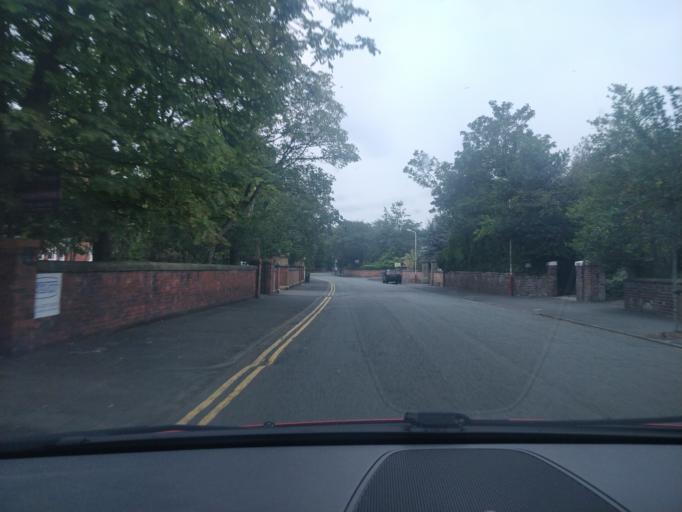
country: GB
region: England
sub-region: Sefton
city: Southport
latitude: 53.6409
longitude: -3.0193
